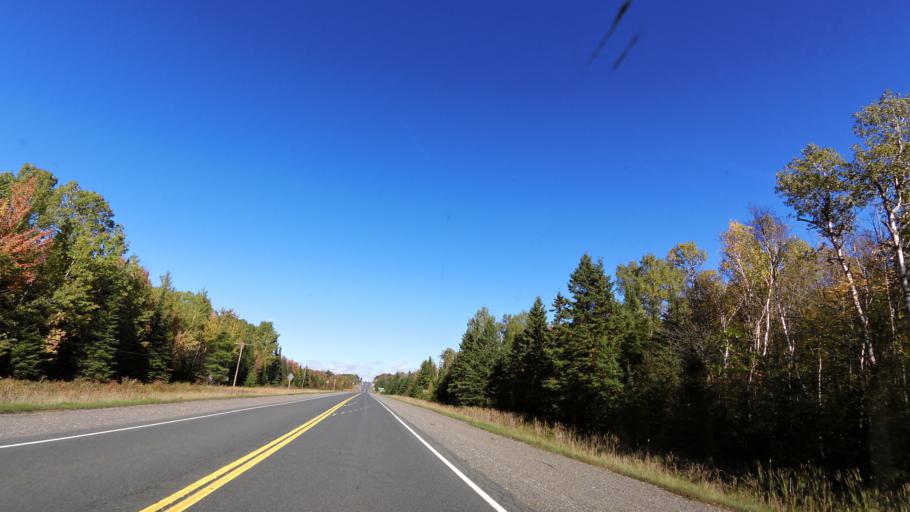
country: CA
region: Ontario
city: Thessalon
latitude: 46.2693
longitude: -83.4446
